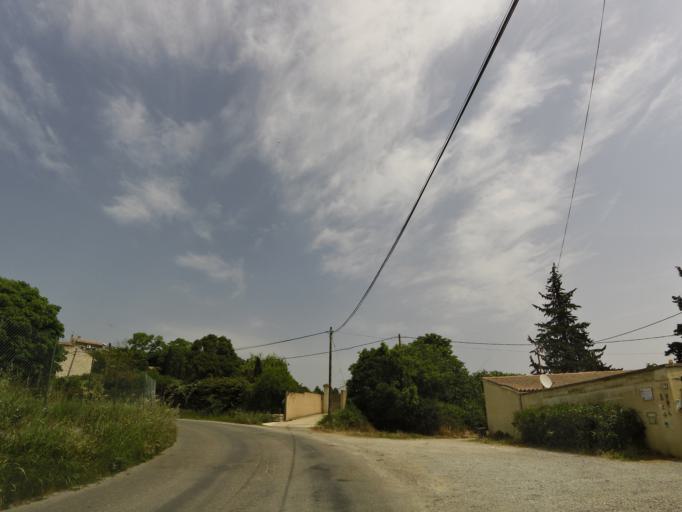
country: FR
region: Languedoc-Roussillon
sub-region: Departement du Gard
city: Aubais
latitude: 43.7680
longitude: 4.1237
